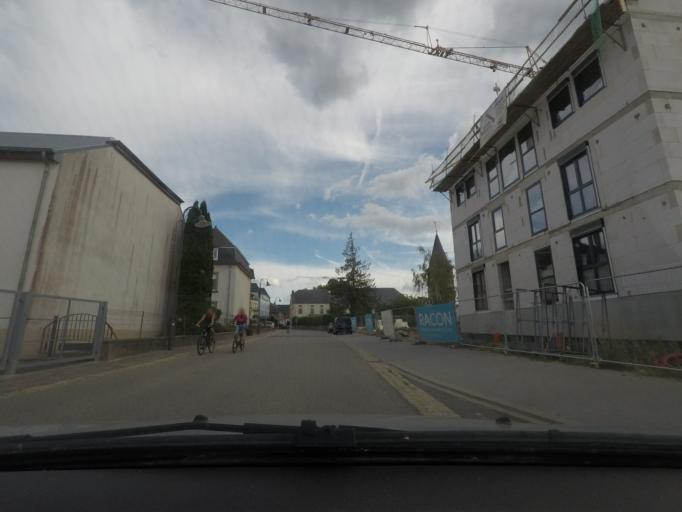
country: LU
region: Grevenmacher
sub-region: Canton d'Echternach
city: Berdorf
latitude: 49.8222
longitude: 6.3484
